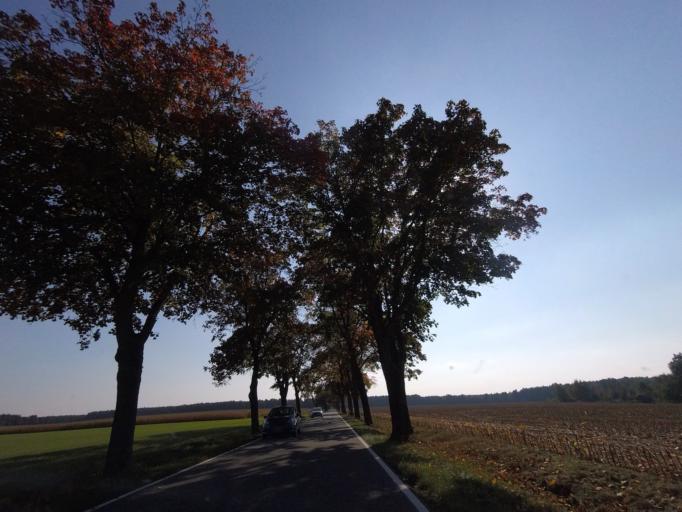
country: DE
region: Brandenburg
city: Niedergorsdorf
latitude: 51.9176
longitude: 13.0285
